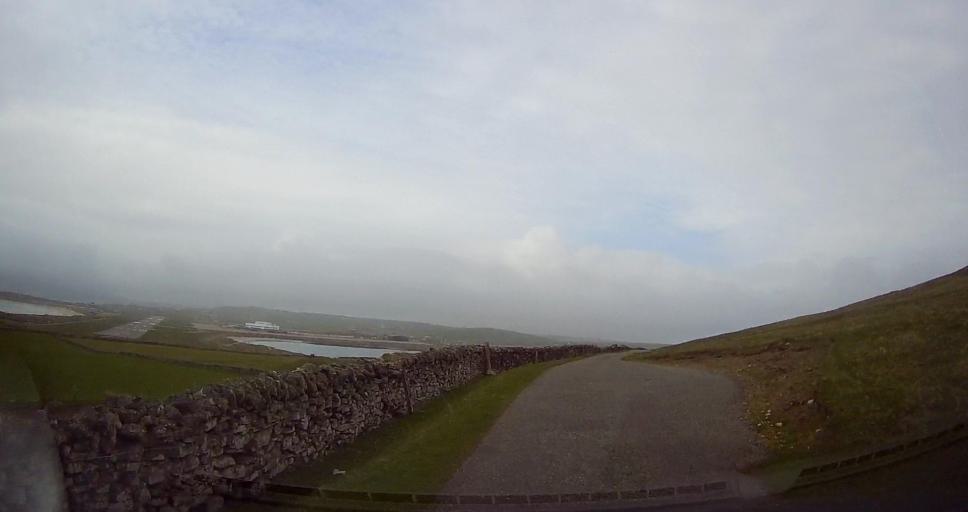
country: GB
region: Scotland
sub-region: Shetland Islands
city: Sandwick
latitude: 59.8680
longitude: -1.2792
